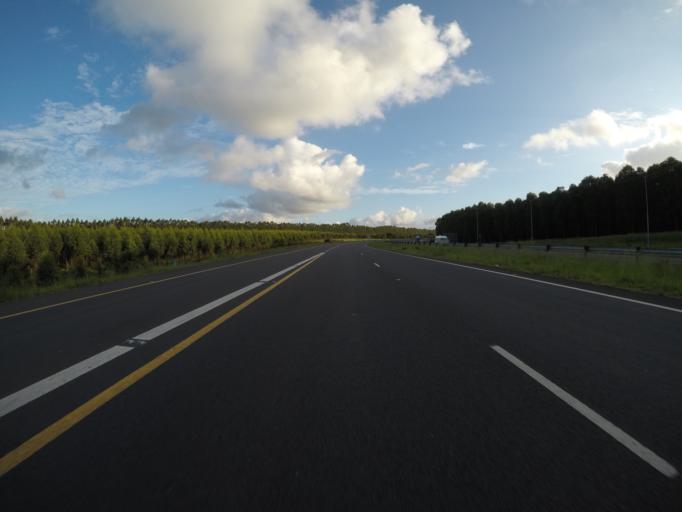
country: ZA
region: KwaZulu-Natal
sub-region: uThungulu District Municipality
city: KwaMbonambi
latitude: -28.5244
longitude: 32.1382
